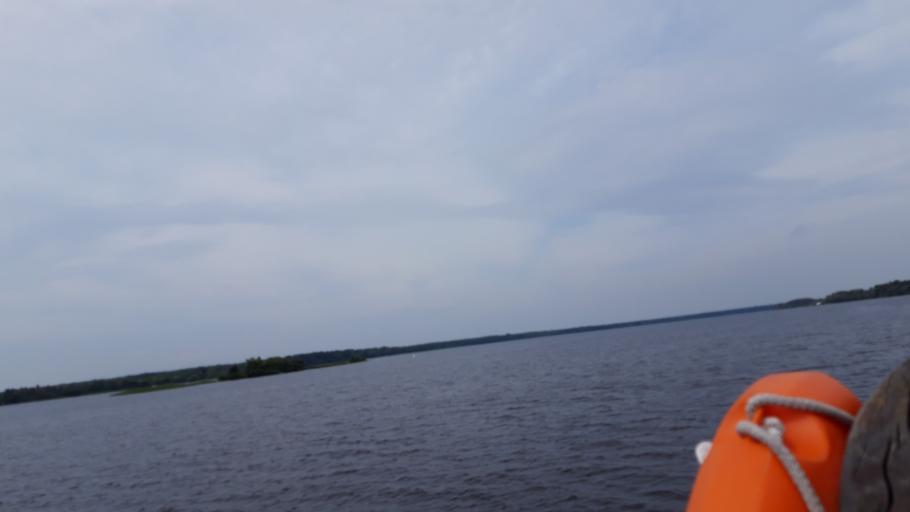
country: RU
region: Tverskaya
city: Konakovo
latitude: 56.7468
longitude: 36.7557
